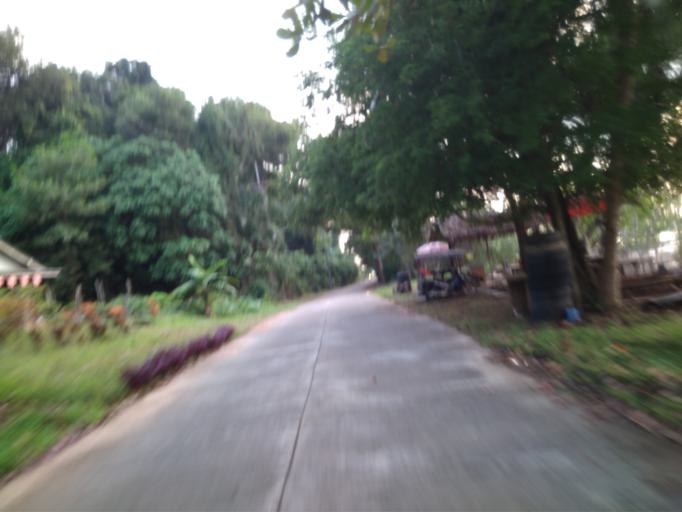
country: TH
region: Phangnga
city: Ko Yao
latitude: 8.1504
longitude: 98.5994
